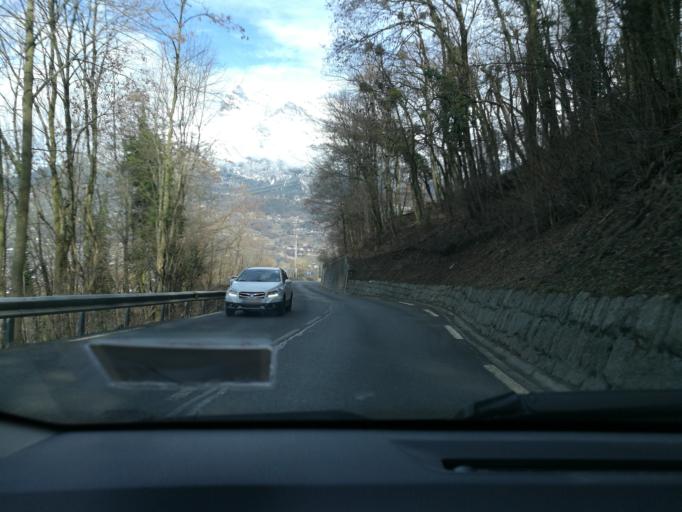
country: FR
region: Rhone-Alpes
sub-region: Departement de la Haute-Savoie
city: Saint-Gervais-les-Bains
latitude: 45.9042
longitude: 6.7133
